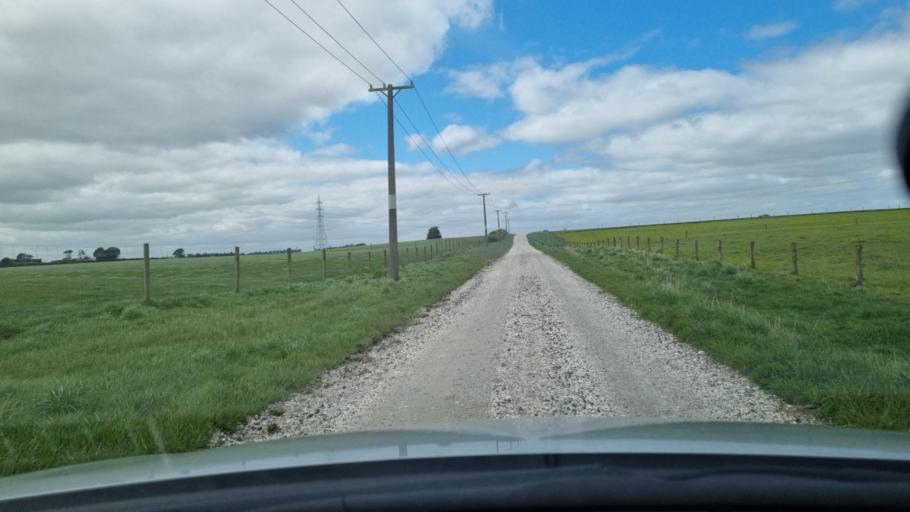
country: NZ
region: Southland
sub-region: Invercargill City
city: Invercargill
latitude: -46.4426
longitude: 168.4457
